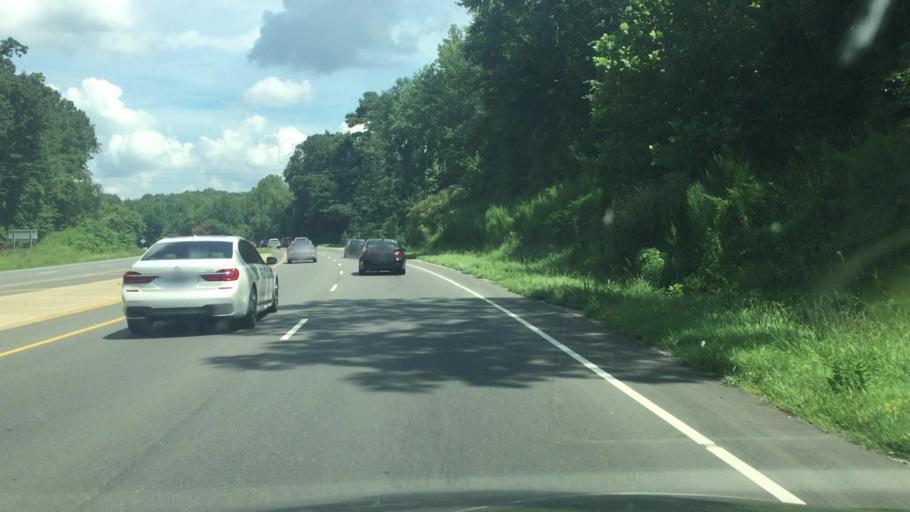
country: US
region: North Carolina
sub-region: Richmond County
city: Rockingham
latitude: 34.9436
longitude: -79.7758
